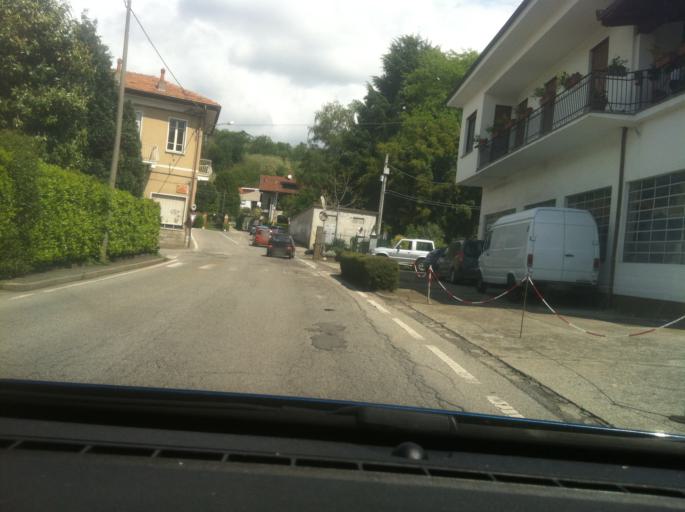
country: IT
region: Piedmont
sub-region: Provincia di Torino
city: Castellamonte
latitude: 45.3846
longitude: 7.7175
